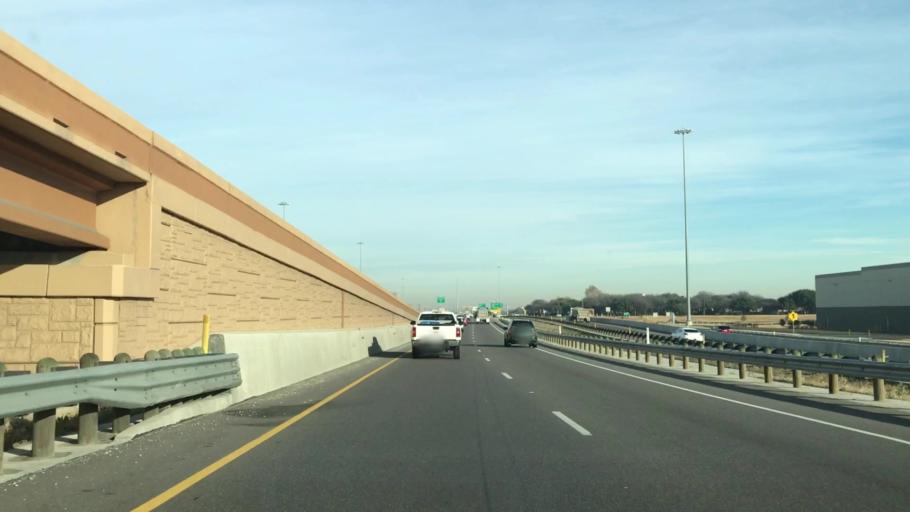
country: US
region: Texas
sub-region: Tarrant County
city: Blue Mound
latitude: 32.8438
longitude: -97.3124
